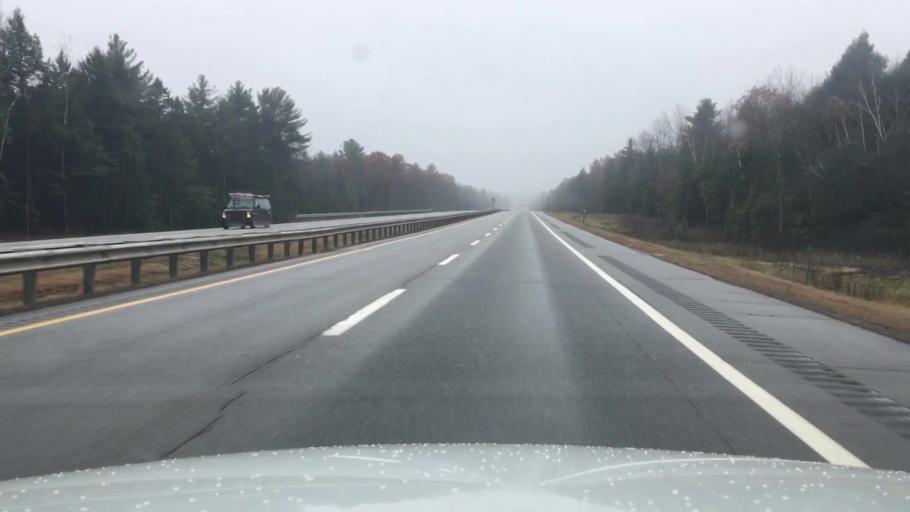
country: US
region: Maine
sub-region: Kennebec County
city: Monmouth
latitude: 44.1377
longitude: -69.9412
